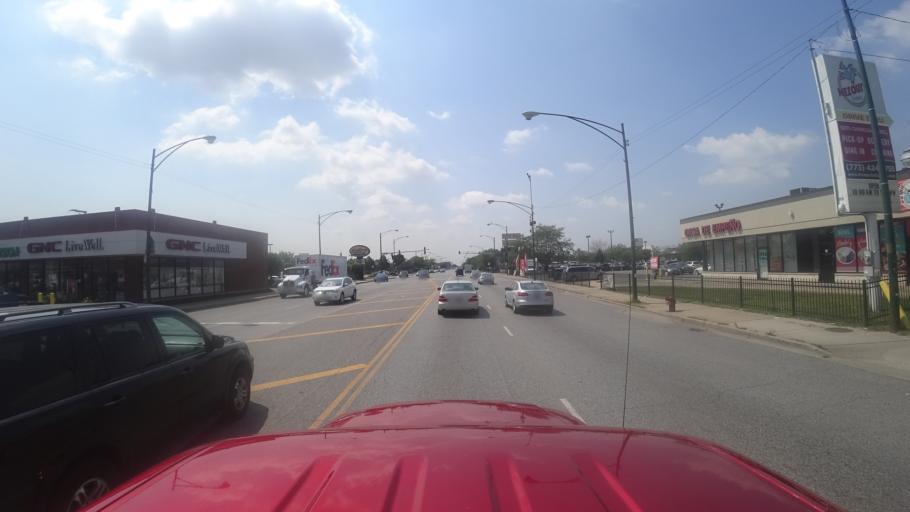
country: US
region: Illinois
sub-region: Cook County
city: Cicero
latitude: 41.7995
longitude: -87.7234
